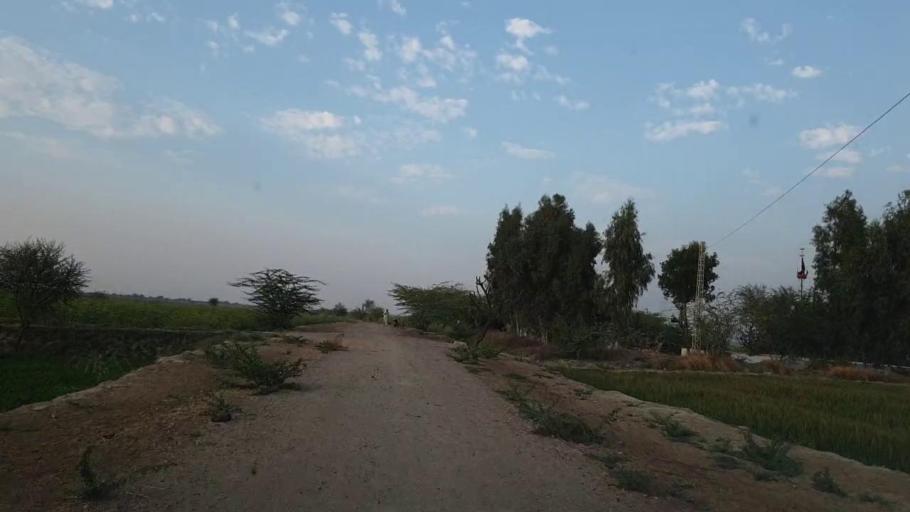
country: PK
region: Sindh
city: Pithoro
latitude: 25.6000
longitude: 69.3100
